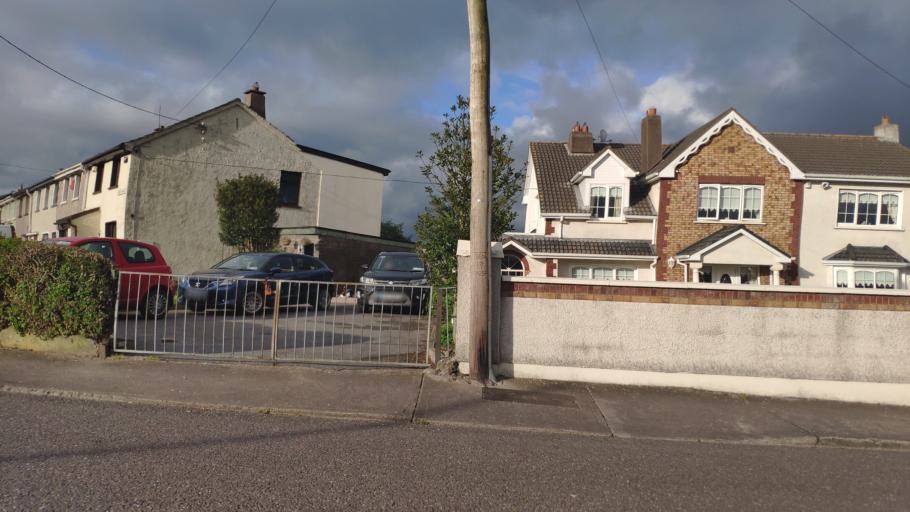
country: IE
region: Munster
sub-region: County Cork
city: Cork
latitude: 51.9116
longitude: -8.4876
